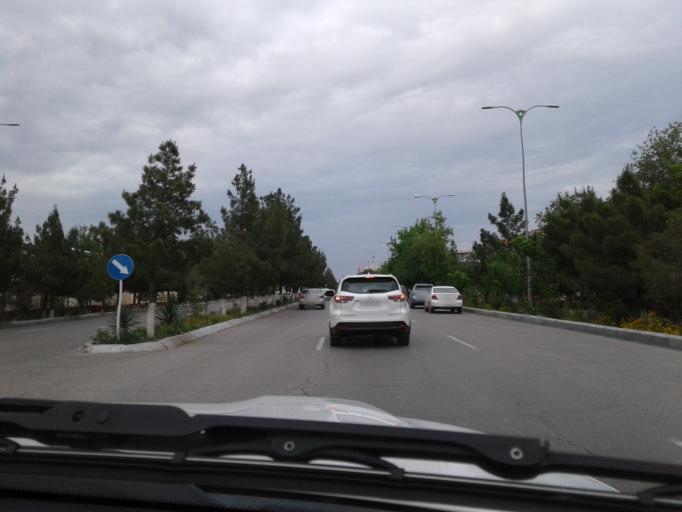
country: TM
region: Mary
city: Mary
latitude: 37.5898
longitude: 61.8681
